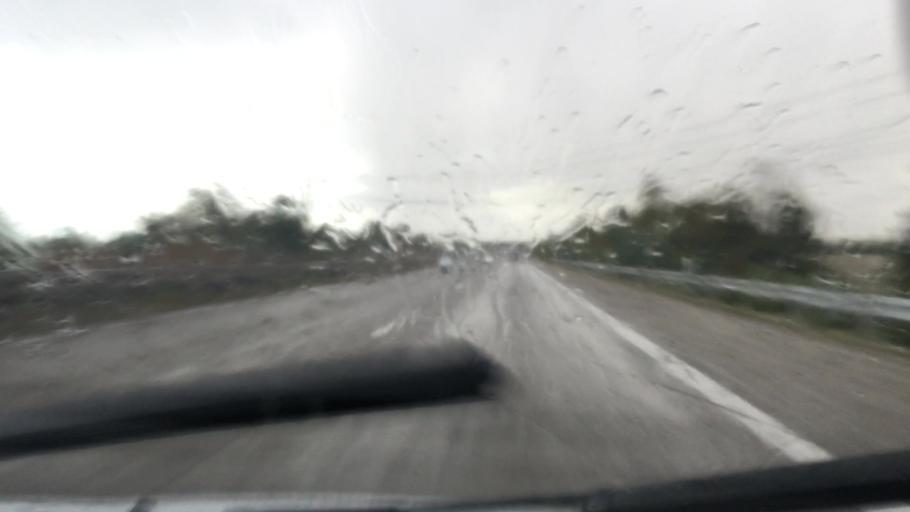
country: DE
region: Saxony-Anhalt
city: Biere
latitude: 51.9831
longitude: 11.6680
